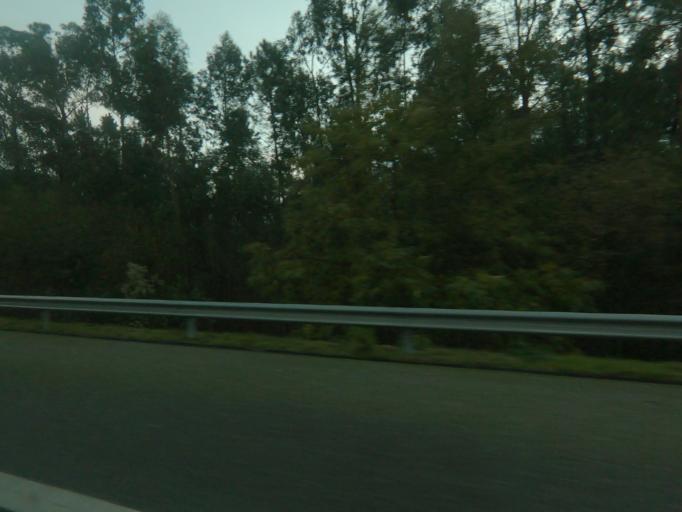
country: PT
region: Braga
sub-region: Barcelos
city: Galegos
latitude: 41.6518
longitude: -8.5503
